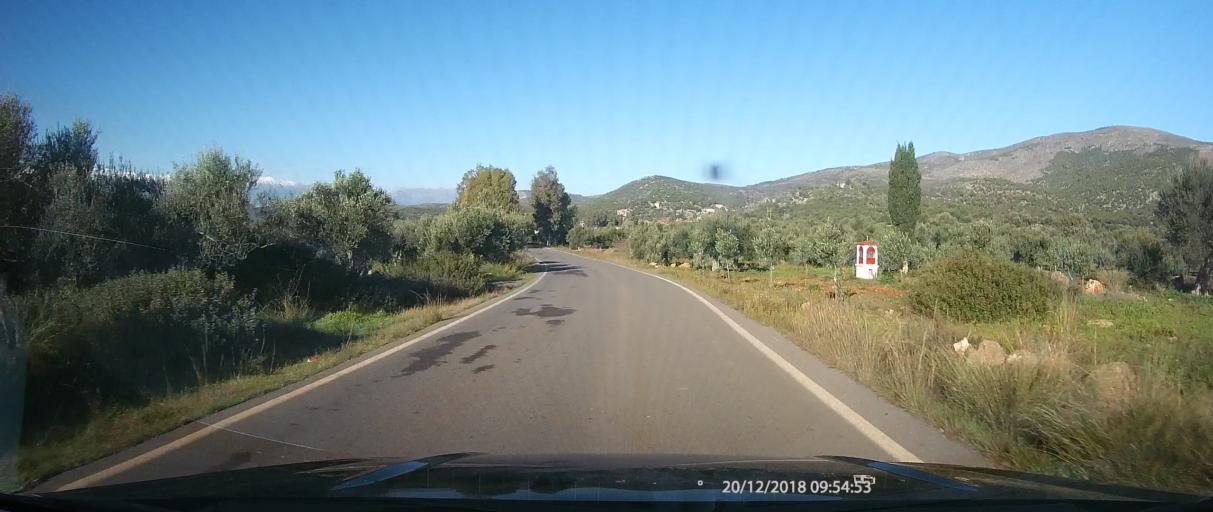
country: GR
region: Peloponnese
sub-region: Nomos Lakonias
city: Yerakion
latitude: 37.0209
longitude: 22.6300
